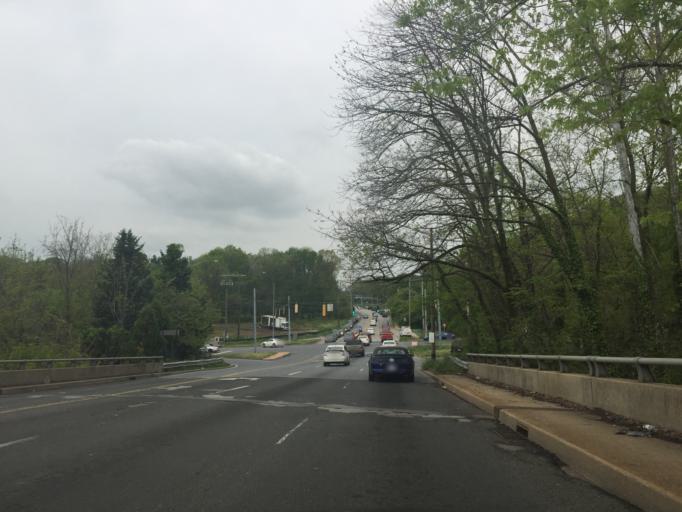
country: US
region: Maryland
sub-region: Baltimore County
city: Woodlawn
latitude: 39.3044
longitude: -76.7120
